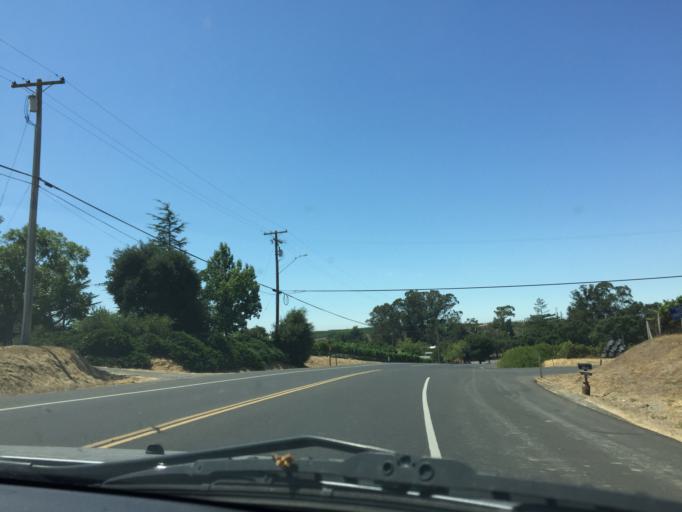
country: US
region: California
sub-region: Napa County
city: Napa
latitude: 38.2581
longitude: -122.3373
